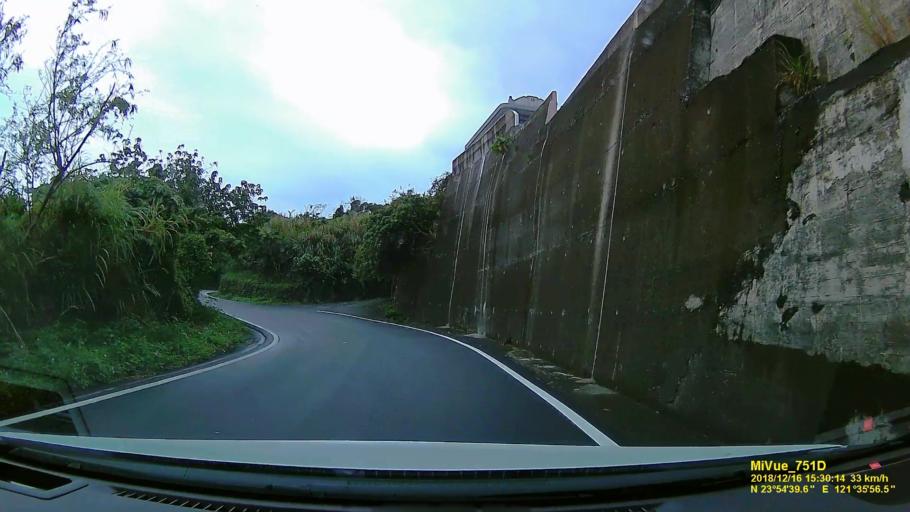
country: TW
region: Taiwan
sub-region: Hualien
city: Hualian
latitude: 23.9111
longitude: 121.5991
